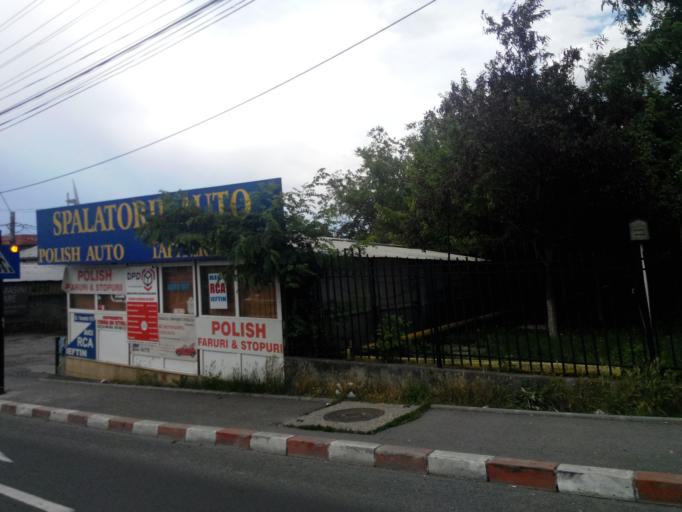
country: RO
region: Arges
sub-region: Comuna Albestii de Arges
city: Pitesti
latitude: 44.8742
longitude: 24.8474
